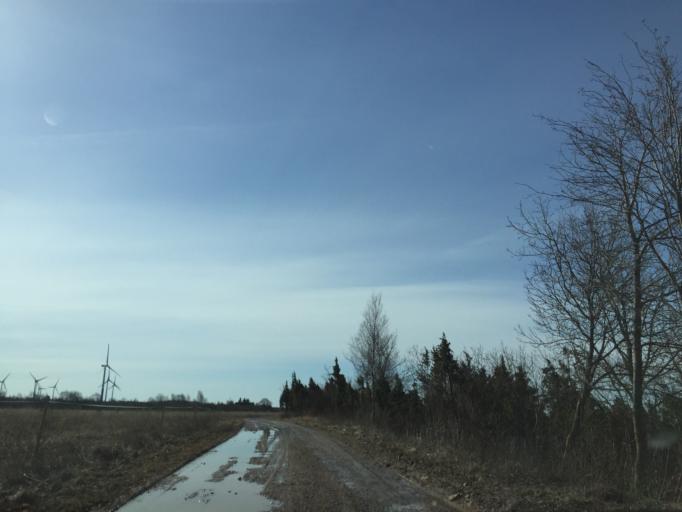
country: EE
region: Laeaene
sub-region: Haapsalu linn
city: Haapsalu
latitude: 58.6521
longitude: 23.5136
